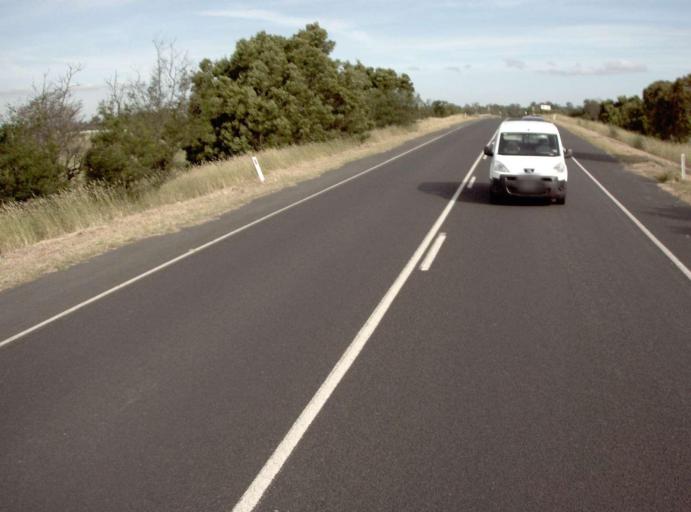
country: AU
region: Victoria
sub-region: Latrobe
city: Traralgon
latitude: -38.1627
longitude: 146.5577
